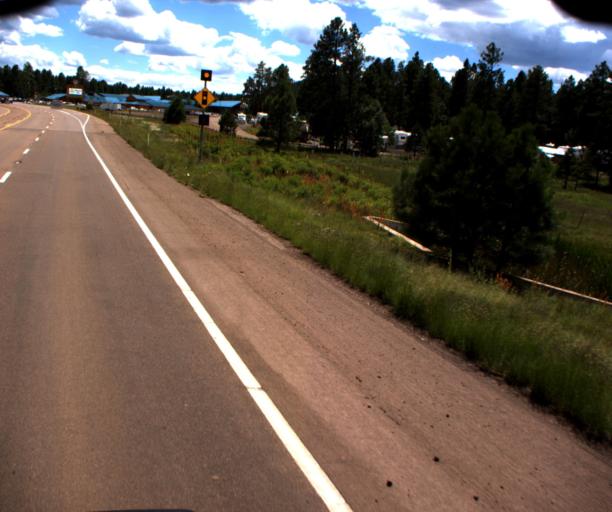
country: US
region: Arizona
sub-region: Navajo County
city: Pinetop-Lakeside
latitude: 34.0824
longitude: -109.9060
